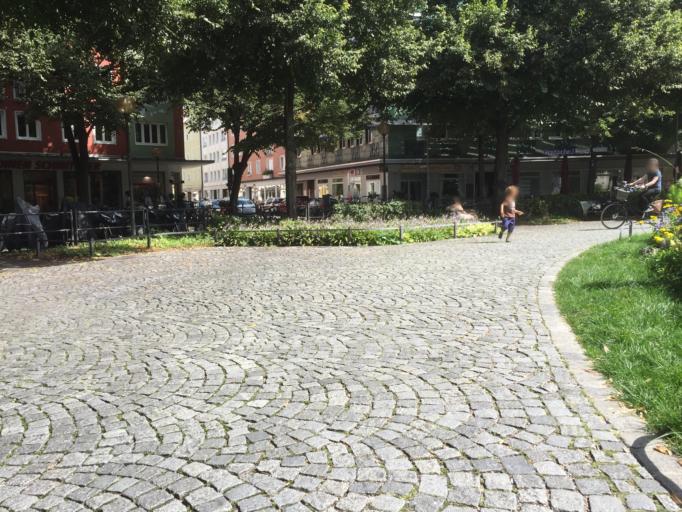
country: DE
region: Bavaria
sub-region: Upper Bavaria
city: Munich
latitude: 48.1287
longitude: 11.5961
